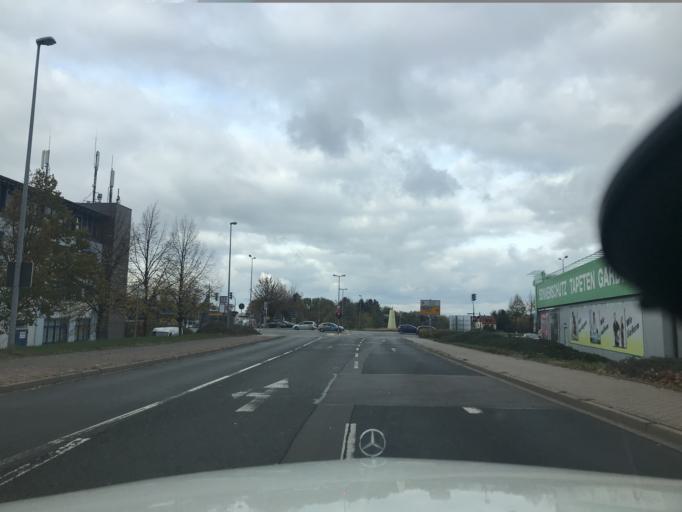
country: DE
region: Thuringia
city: Erfurt
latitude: 50.9769
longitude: 11.0864
